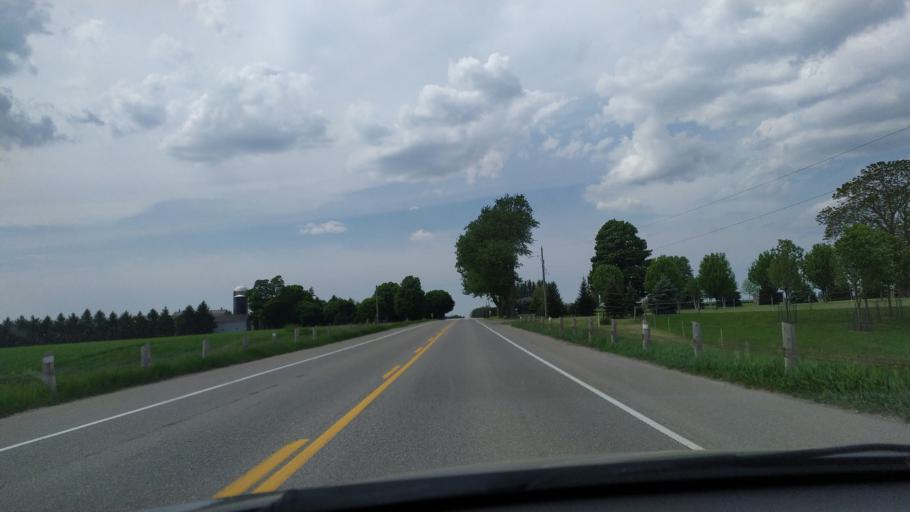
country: CA
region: Ontario
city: Dorchester
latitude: 43.1775
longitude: -81.0497
